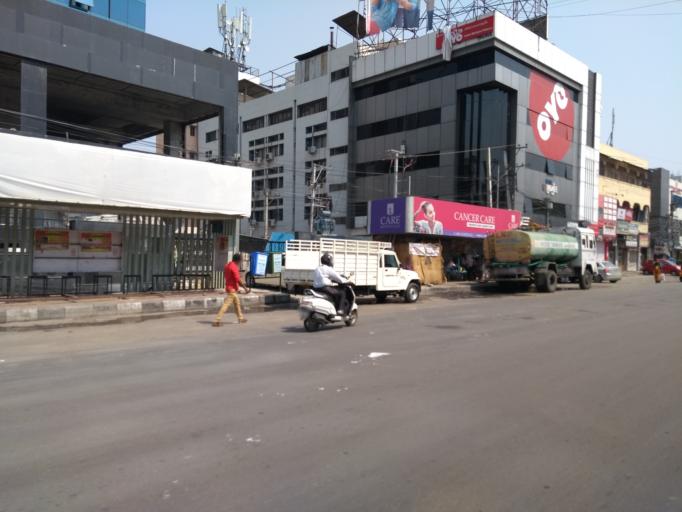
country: IN
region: Telangana
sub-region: Hyderabad
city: Malkajgiri
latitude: 17.4312
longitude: 78.4882
